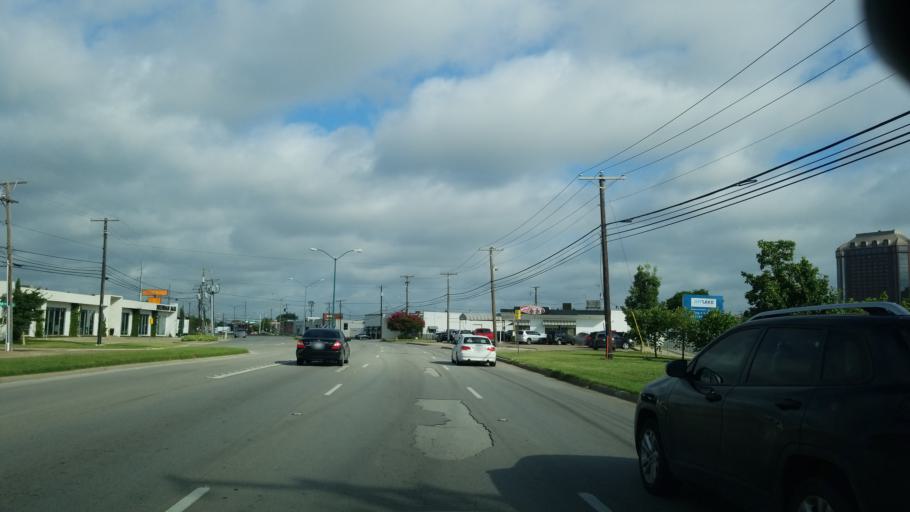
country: US
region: Texas
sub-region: Dallas County
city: Dallas
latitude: 32.7946
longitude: -96.8273
